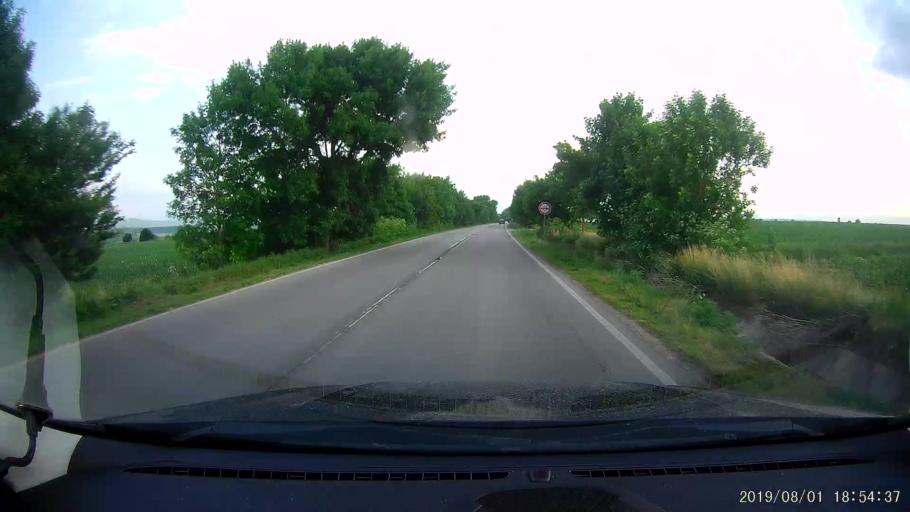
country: BG
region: Shumen
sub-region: Obshtina Shumen
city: Shumen
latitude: 43.1944
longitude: 27.0027
